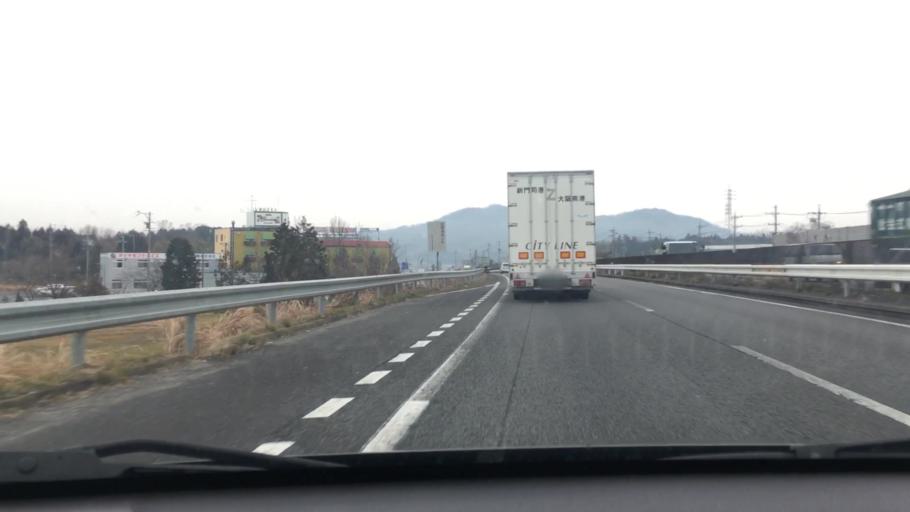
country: JP
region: Mie
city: Ueno-ebisumachi
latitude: 34.7610
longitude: 136.1530
